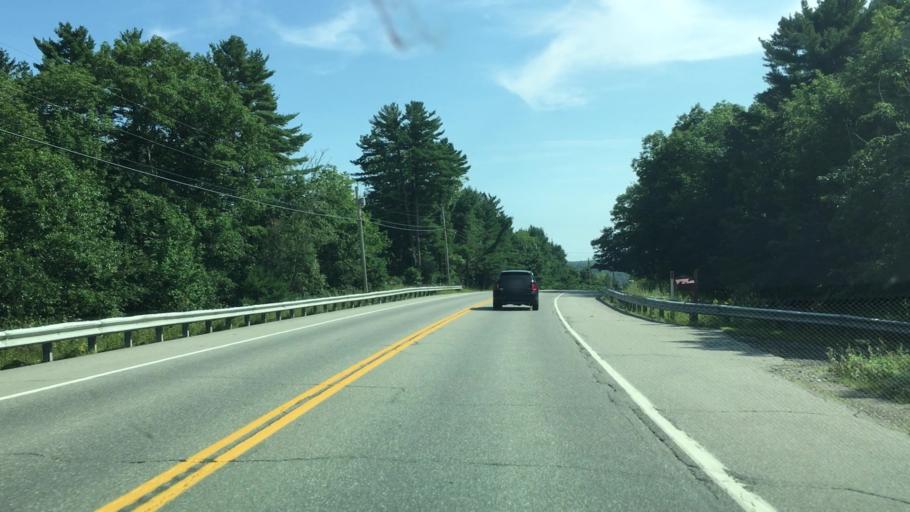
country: US
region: Maine
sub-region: Waldo County
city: Winterport
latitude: 44.6652
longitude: -68.8314
